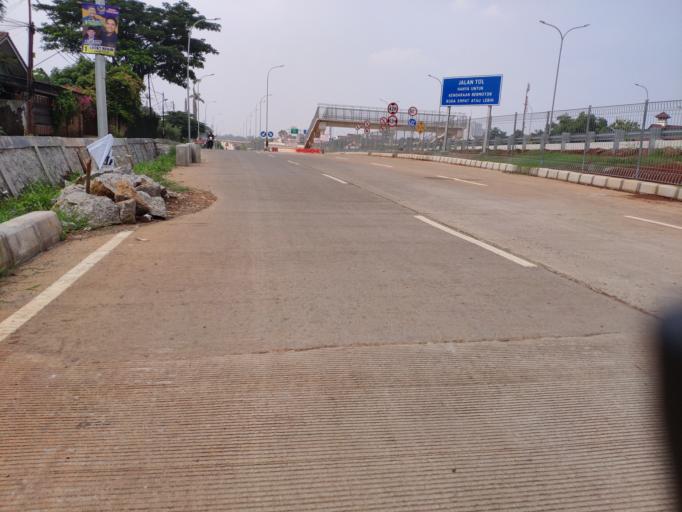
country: ID
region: West Java
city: Pamulang
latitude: -6.3268
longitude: 106.8017
